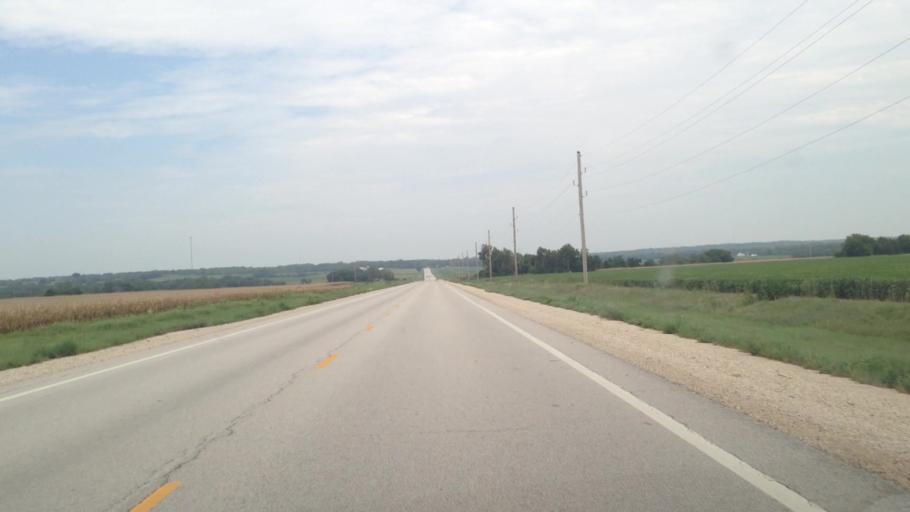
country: US
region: Kansas
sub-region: Anderson County
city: Garnett
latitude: 38.0592
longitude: -95.1693
